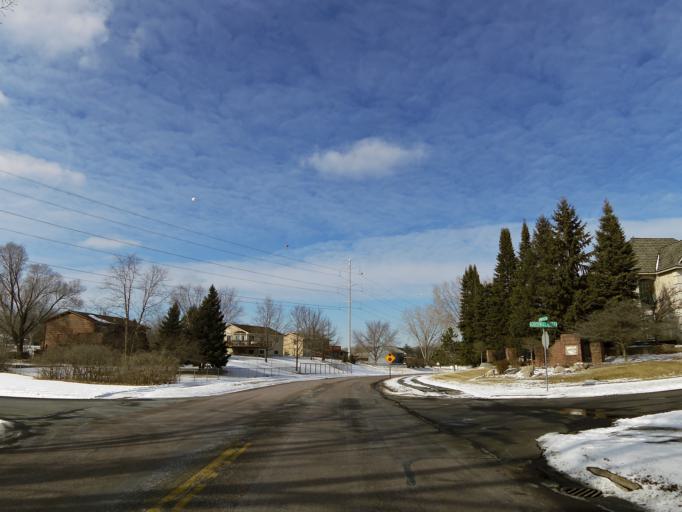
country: US
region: Minnesota
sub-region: Hennepin County
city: Eden Prairie
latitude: 44.8186
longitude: -93.4286
